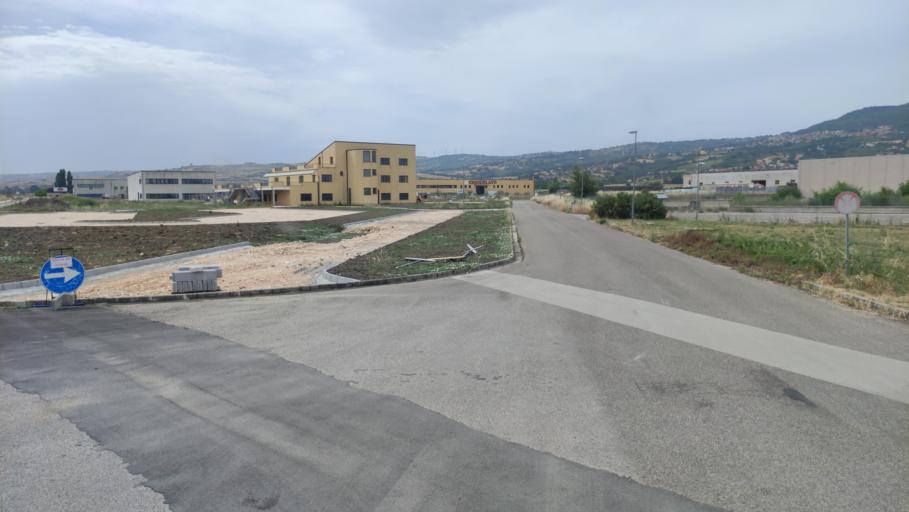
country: IT
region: Campania
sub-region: Provincia di Avellino
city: Sturno
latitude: 41.0511
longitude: 15.1216
